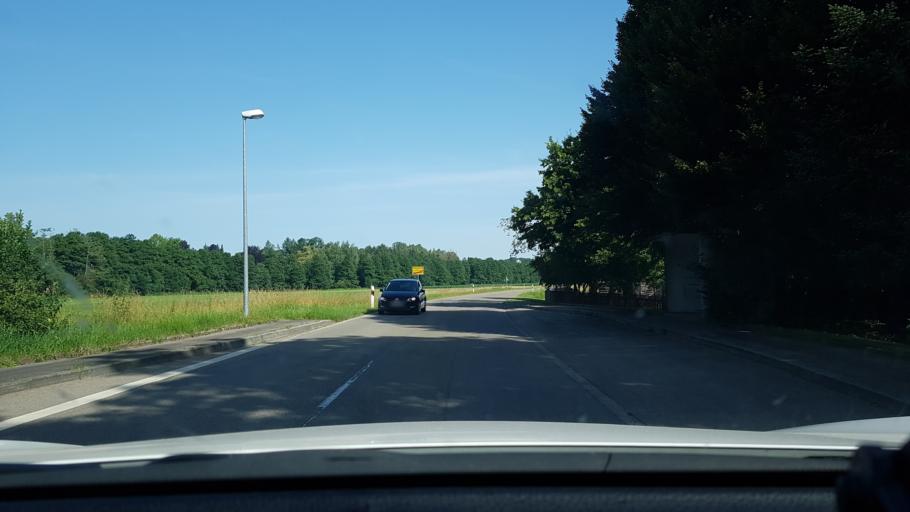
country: DE
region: Baden-Wuerttemberg
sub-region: Tuebingen Region
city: Schwendi
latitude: 48.1903
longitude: 9.9642
